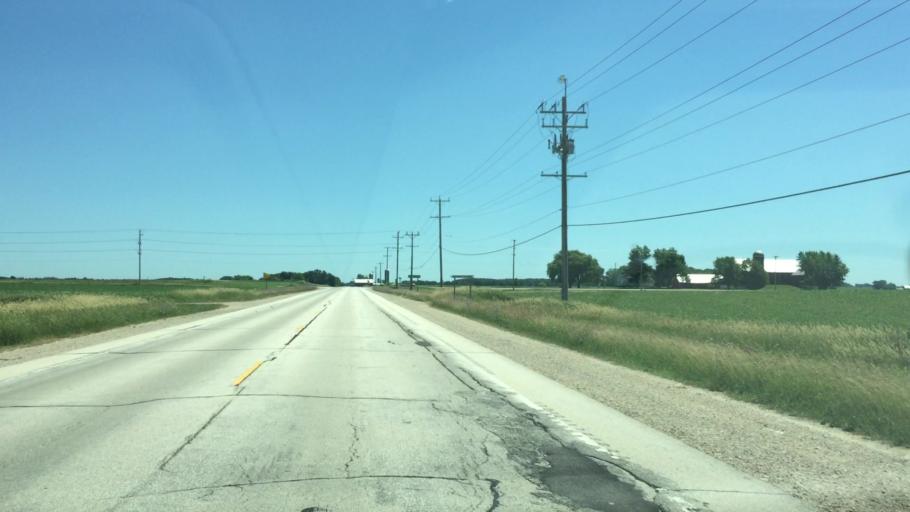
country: US
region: Wisconsin
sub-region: Calumet County
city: Hilbert
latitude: 44.1404
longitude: -88.2079
